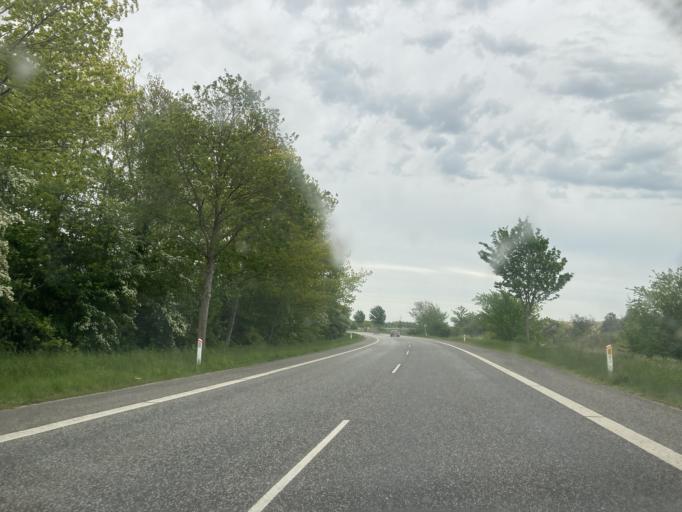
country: DK
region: Zealand
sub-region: Roskilde Kommune
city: Svogerslev
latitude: 55.6290
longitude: 12.0263
